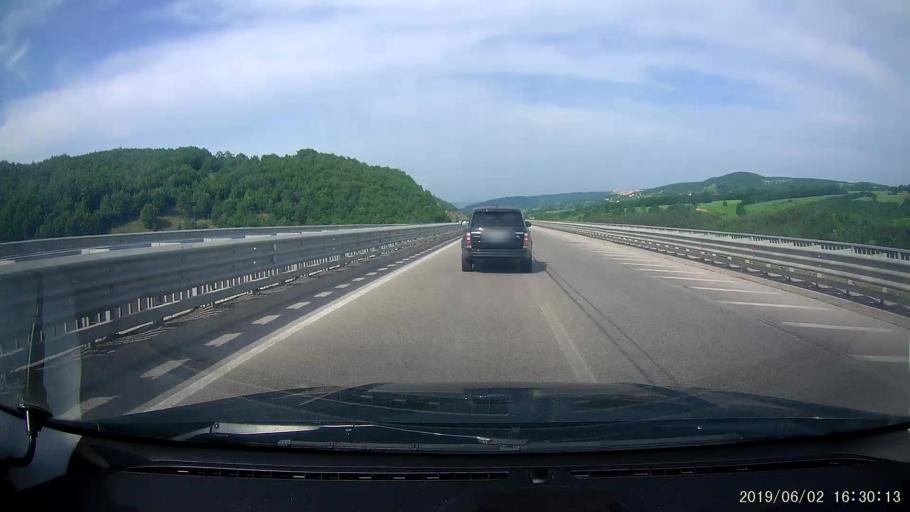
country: TR
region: Samsun
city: Ladik
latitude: 41.0235
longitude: 35.8777
